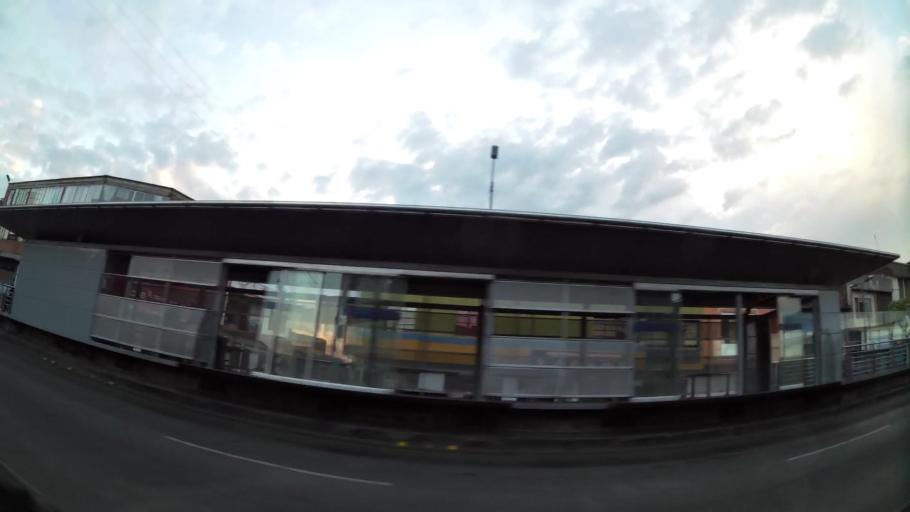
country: CO
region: Valle del Cauca
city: Cali
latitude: 3.4434
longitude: -76.5266
